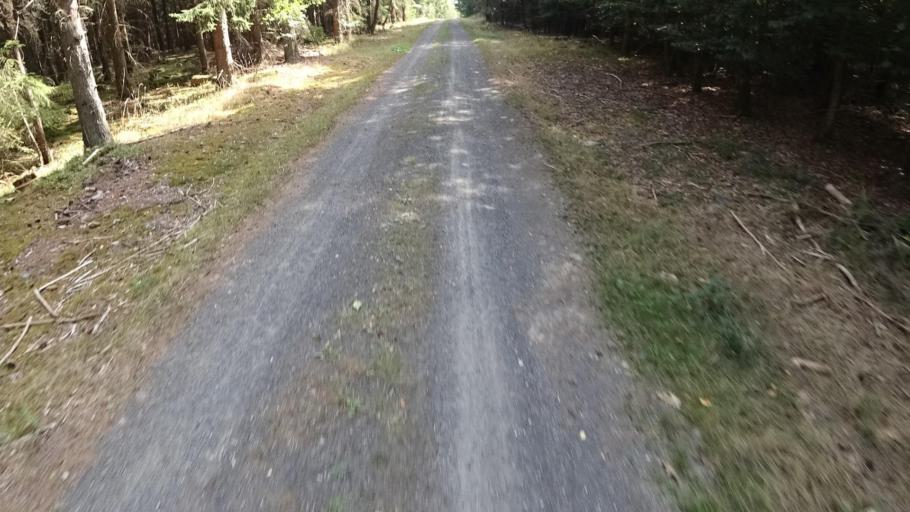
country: DE
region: Rheinland-Pfalz
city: Kisselbach
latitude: 50.0673
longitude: 7.6192
